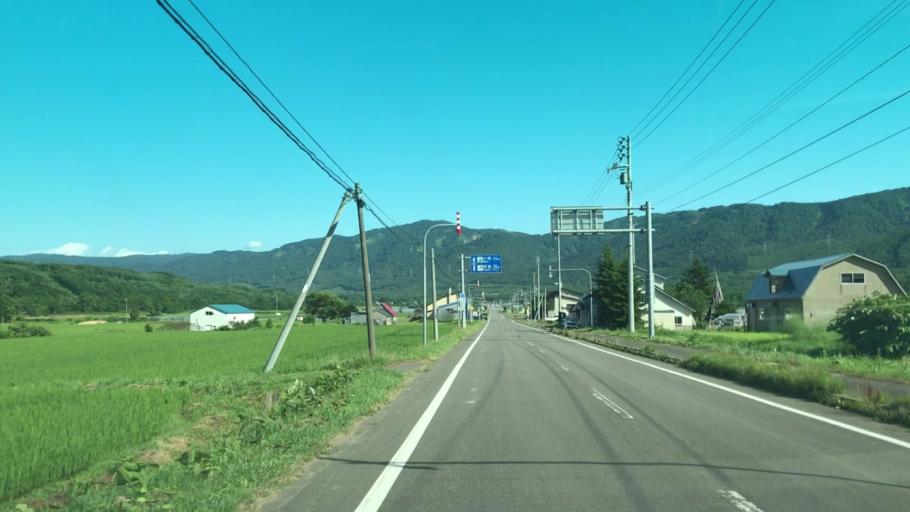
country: JP
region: Hokkaido
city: Yoichi
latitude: 43.0552
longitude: 140.7179
